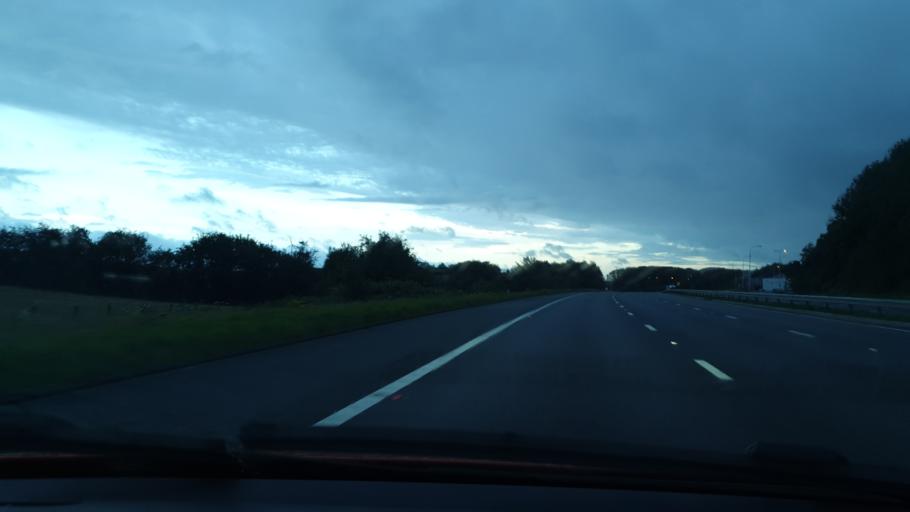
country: GB
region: England
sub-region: Cumbria
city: Milnthorpe
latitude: 54.1810
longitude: -2.7301
